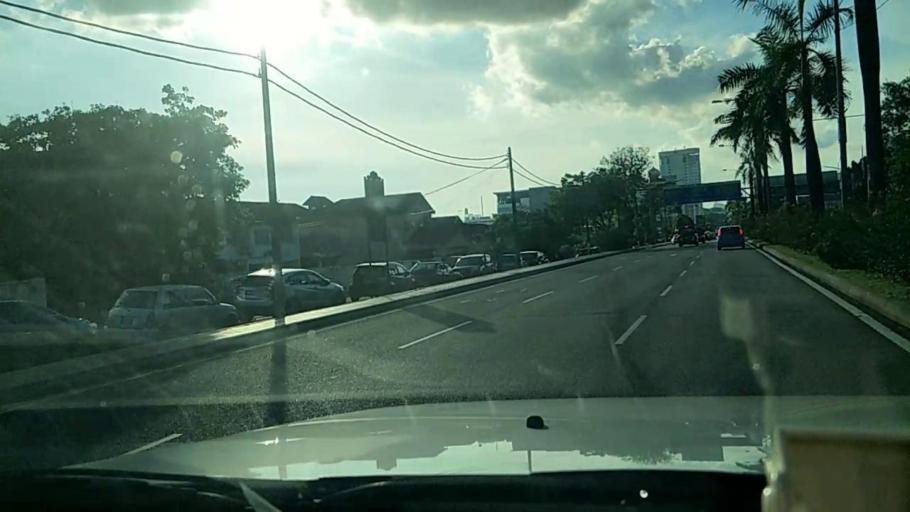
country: MY
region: Selangor
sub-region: Petaling
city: Petaling Jaya
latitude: 3.1110
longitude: 101.6360
